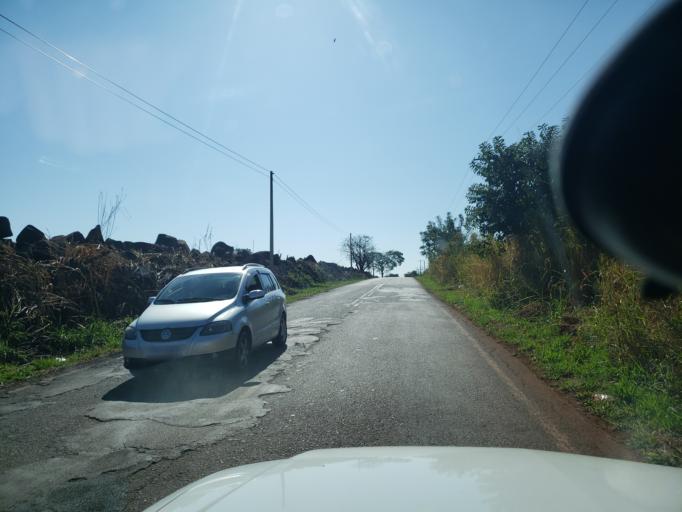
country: BR
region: Sao Paulo
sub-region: Moji-Guacu
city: Mogi-Gaucu
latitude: -22.3415
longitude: -46.8885
